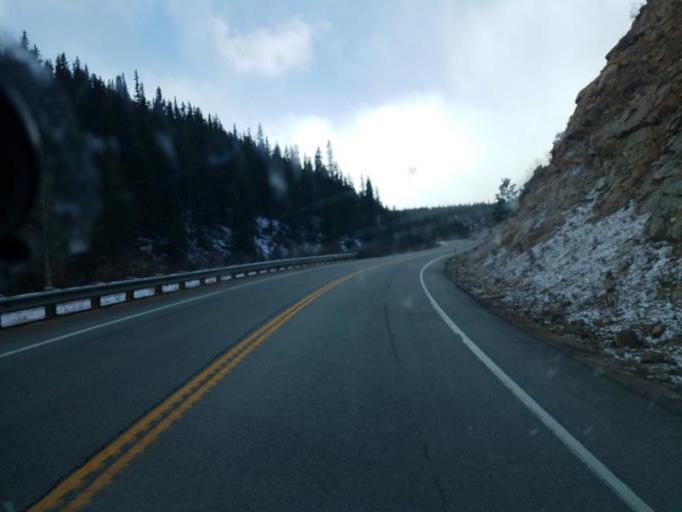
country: US
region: Colorado
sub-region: Clear Creek County
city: Georgetown
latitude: 39.4447
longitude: -105.7406
